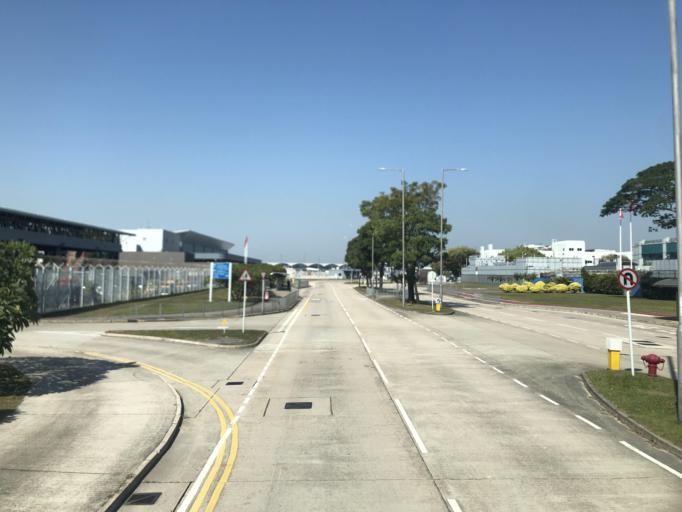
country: HK
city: Tai O
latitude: 22.3011
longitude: 113.9313
